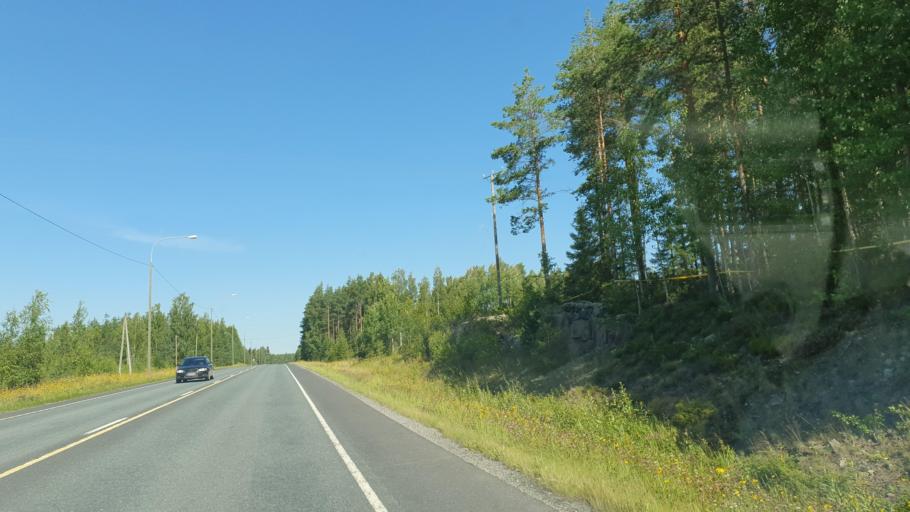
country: FI
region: Northern Savo
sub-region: Kuopio
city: Siilinjaervi
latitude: 63.1698
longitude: 27.5592
